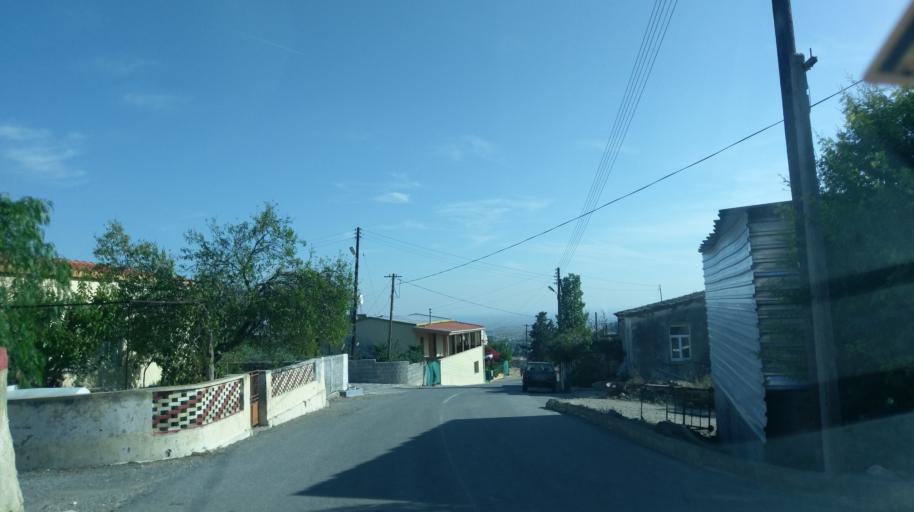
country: CY
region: Ammochostos
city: Lefkonoiko
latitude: 35.3468
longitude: 33.7991
